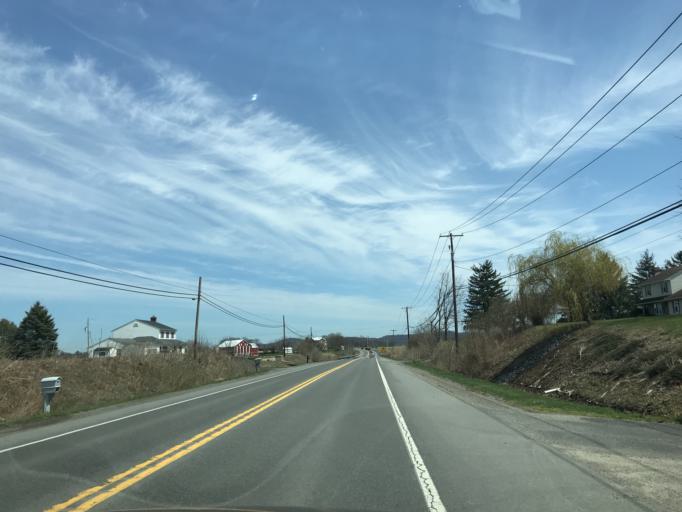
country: US
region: Pennsylvania
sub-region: Snyder County
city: Selinsgrove
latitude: 40.8052
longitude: -76.8972
